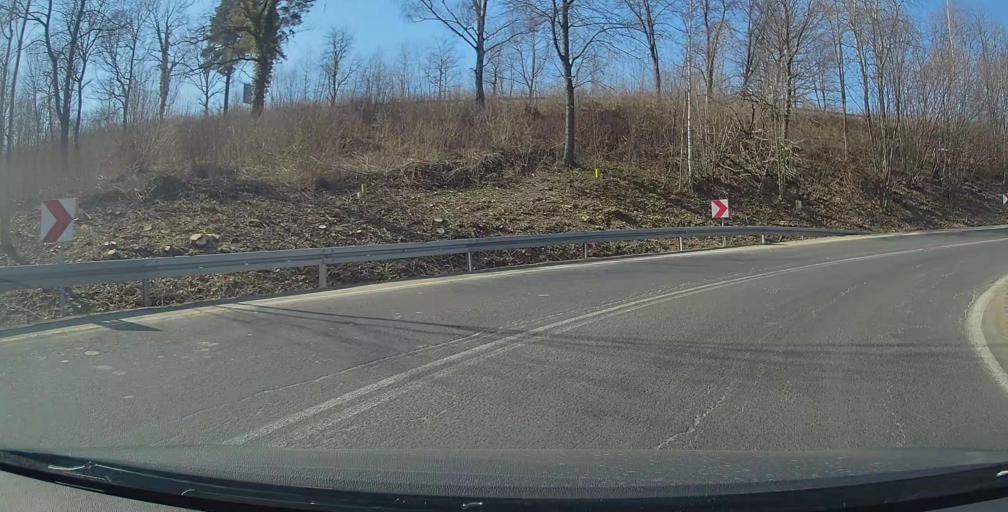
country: PL
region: Subcarpathian Voivodeship
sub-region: Powiat przemyski
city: Bircza
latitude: 49.6531
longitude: 22.4240
